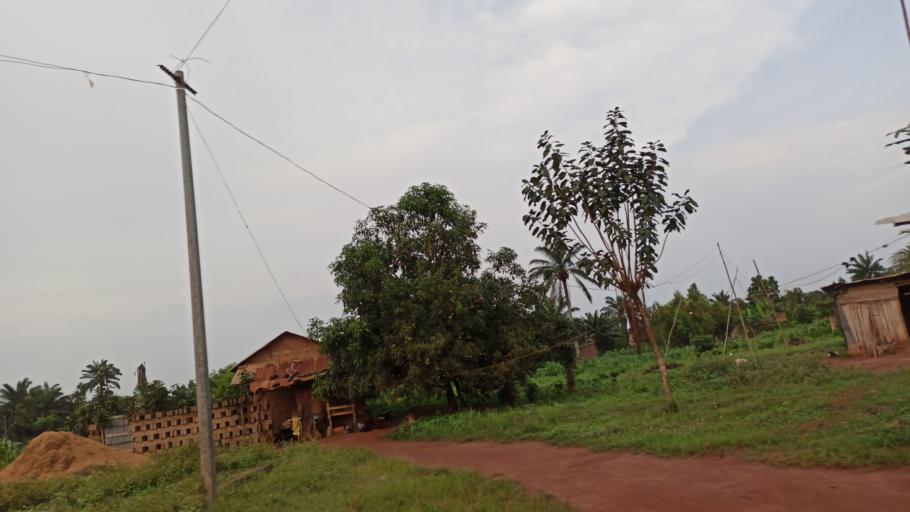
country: BJ
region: Queme
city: Porto-Novo
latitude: 6.5188
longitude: 2.6765
